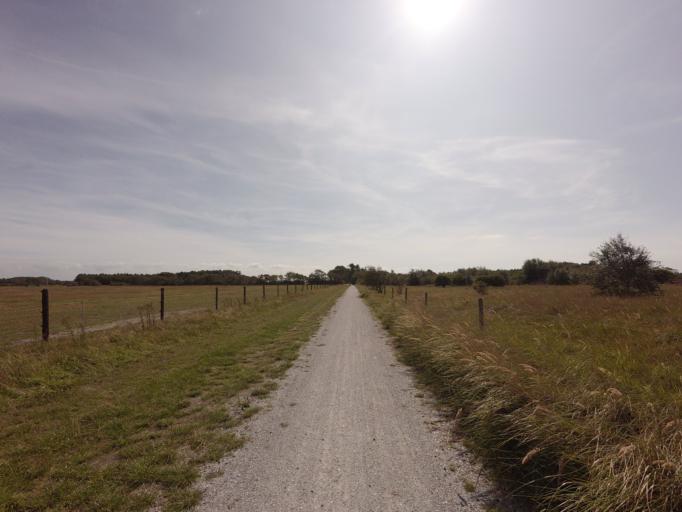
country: NL
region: Friesland
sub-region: Gemeente Ameland
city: Hollum
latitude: 53.4469
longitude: 5.6554
